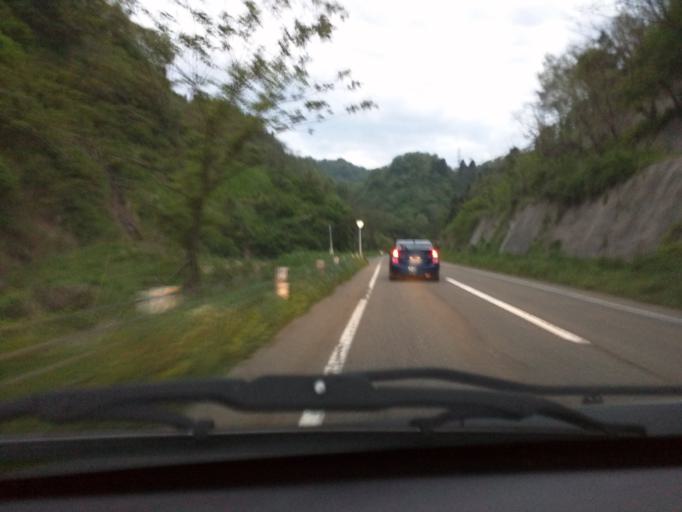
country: JP
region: Niigata
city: Ojiya
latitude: 37.3235
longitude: 138.6788
